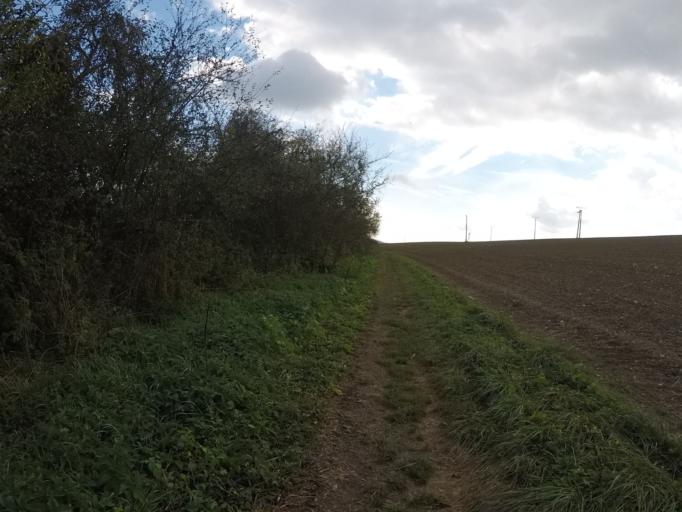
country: SK
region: Presovsky
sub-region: Okres Presov
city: Presov
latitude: 48.9315
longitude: 21.1809
